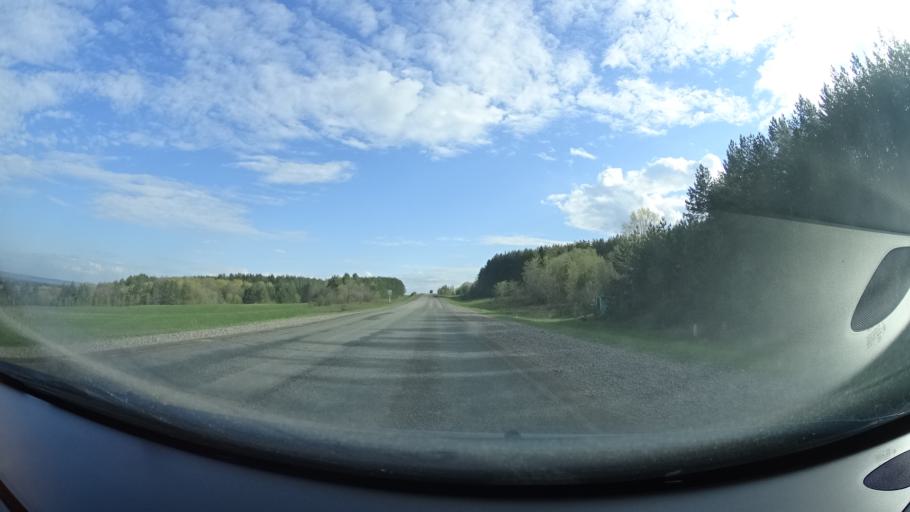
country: RU
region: Bashkortostan
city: Blagoveshchensk
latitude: 55.1376
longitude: 55.8459
